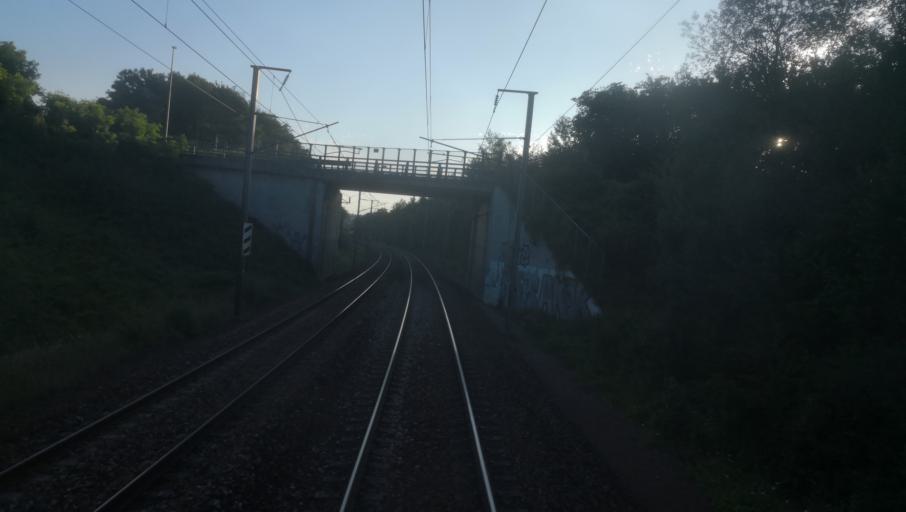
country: FR
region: Lower Normandy
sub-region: Departement du Calvados
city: Beuvillers
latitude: 49.1264
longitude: 0.2842
